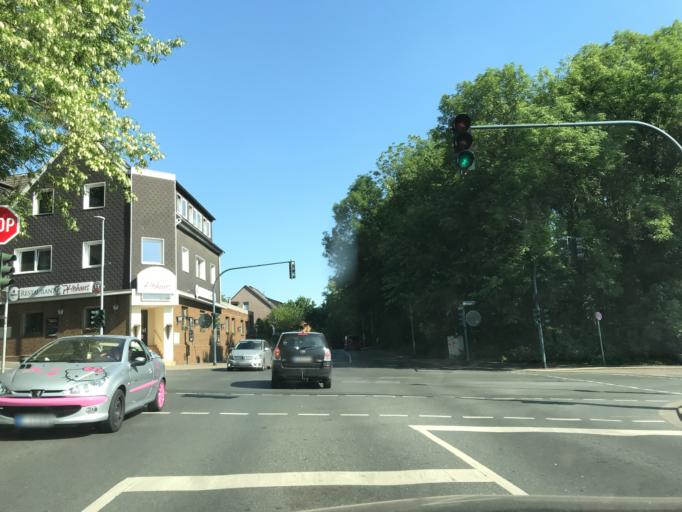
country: DE
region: North Rhine-Westphalia
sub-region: Regierungsbezirk Dusseldorf
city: Essen
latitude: 51.4727
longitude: 7.0685
